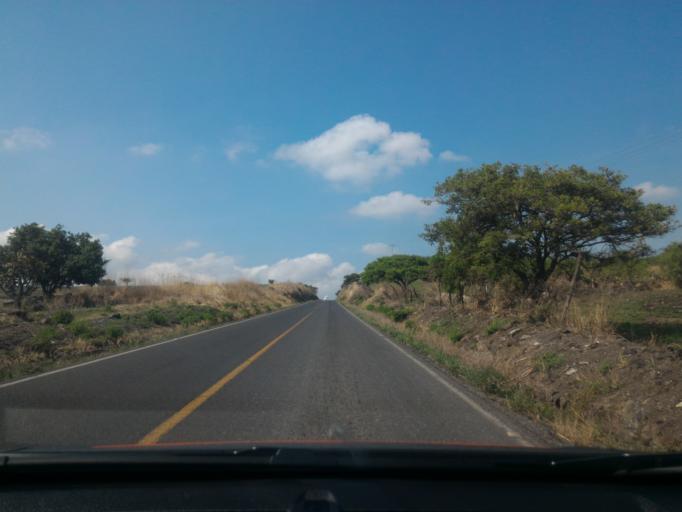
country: MX
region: Guanajuato
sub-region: Penjamo
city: Estacion la Piedad
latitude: 20.4338
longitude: -101.9892
